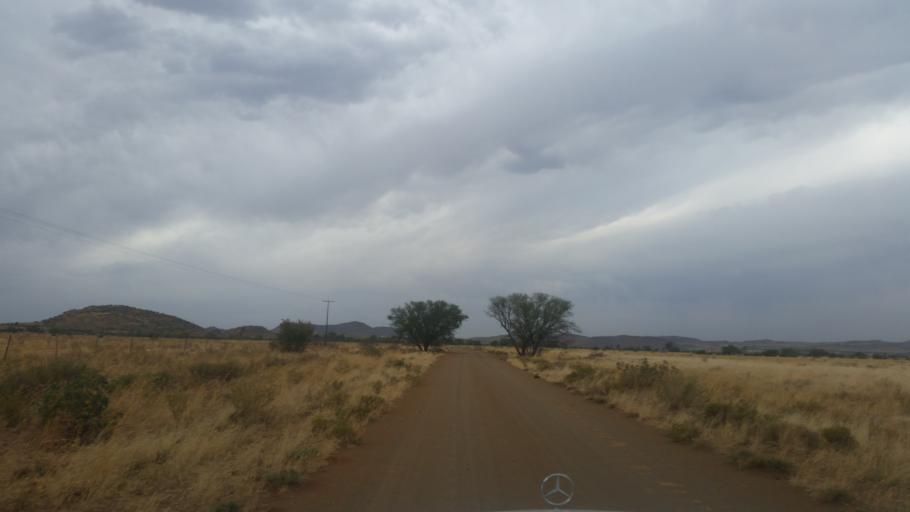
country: ZA
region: Orange Free State
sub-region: Xhariep District Municipality
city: Trompsburg
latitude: -30.5033
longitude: 25.9493
